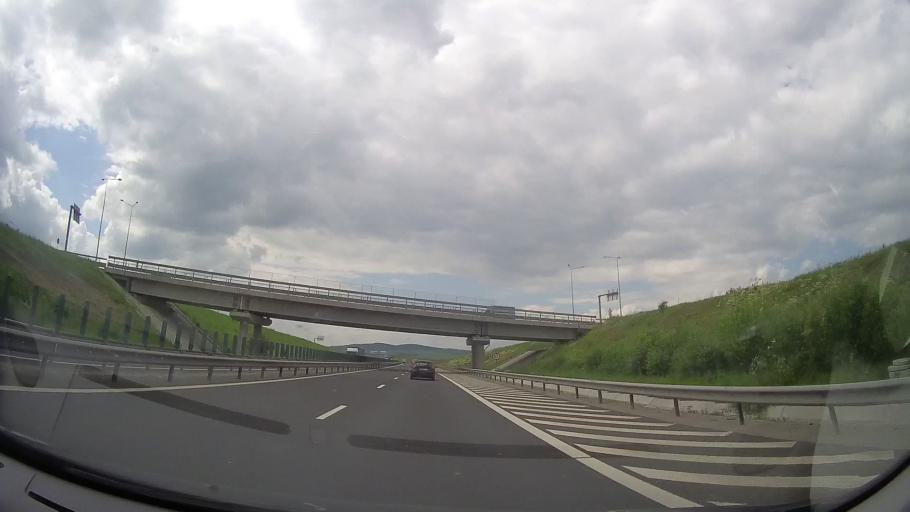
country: RO
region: Alba
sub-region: Comuna Garbova
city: Garbova
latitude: 45.9189
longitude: 23.7217
